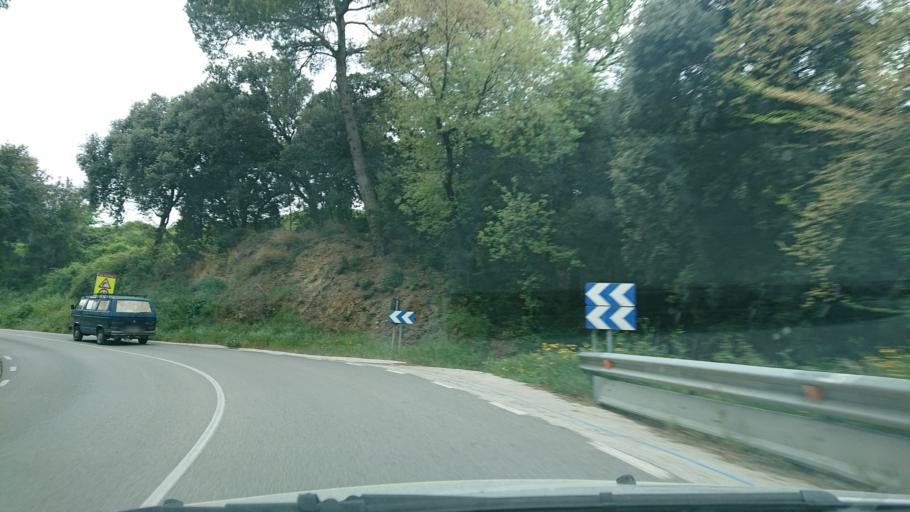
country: ES
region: Catalonia
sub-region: Provincia de Barcelona
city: Sant Pere de Vilamajor
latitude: 41.6761
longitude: 2.3787
